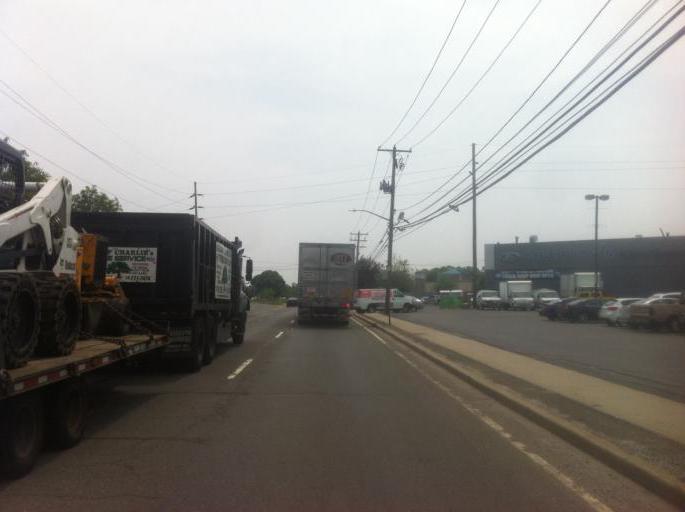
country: US
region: New York
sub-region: Nassau County
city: Bethpage
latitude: 40.7450
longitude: -73.4994
